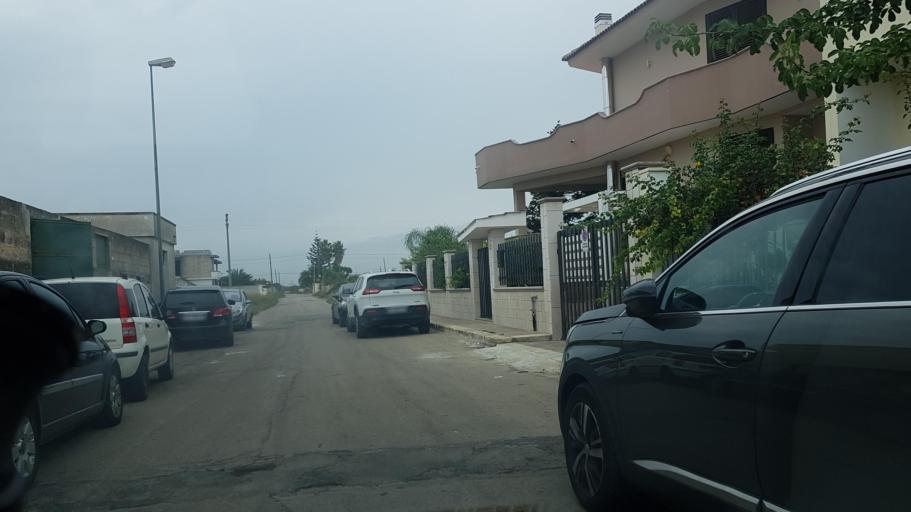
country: IT
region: Apulia
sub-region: Provincia di Brindisi
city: Cellino San Marco
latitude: 40.4743
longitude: 17.9595
